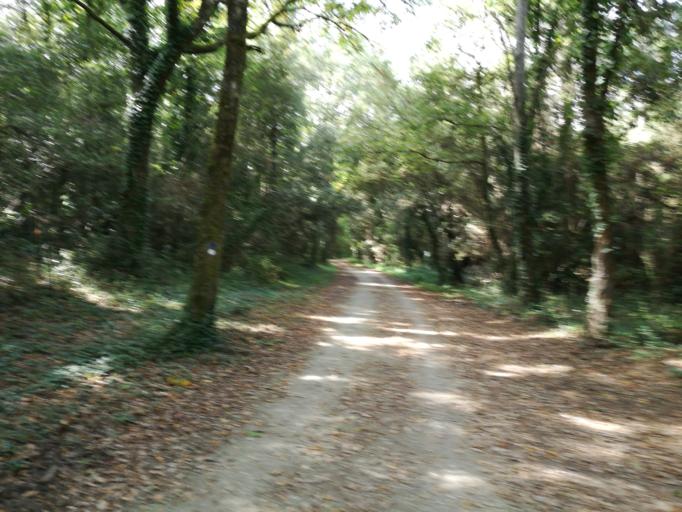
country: FR
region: Poitou-Charentes
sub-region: Departement de la Charente-Maritime
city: Boyard-Ville
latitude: 45.9806
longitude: -1.2869
